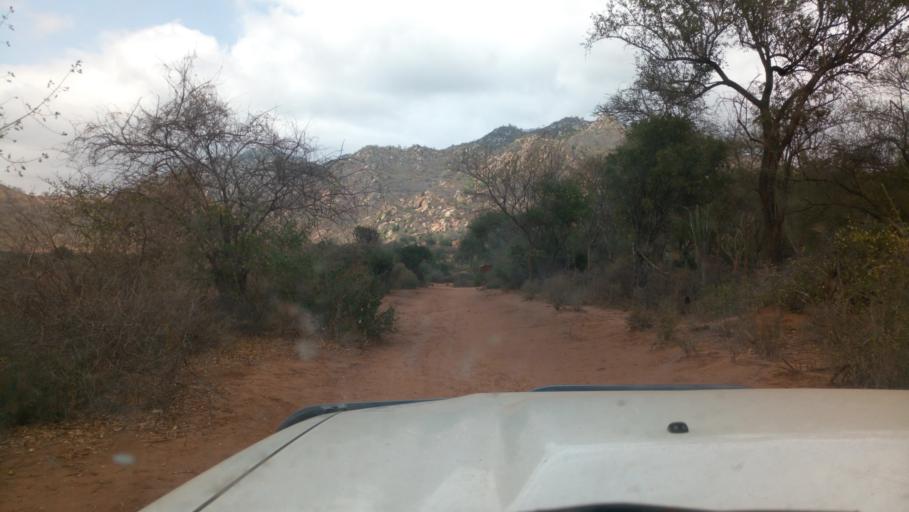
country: KE
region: Kitui
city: Kitui
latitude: -1.8545
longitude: 38.3422
